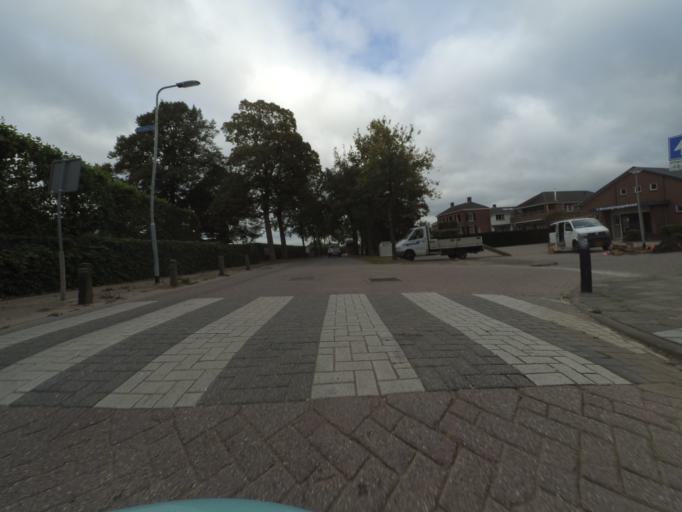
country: NL
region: Gelderland
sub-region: Gemeente Buren
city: Lienden
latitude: 51.9607
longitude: 5.4884
